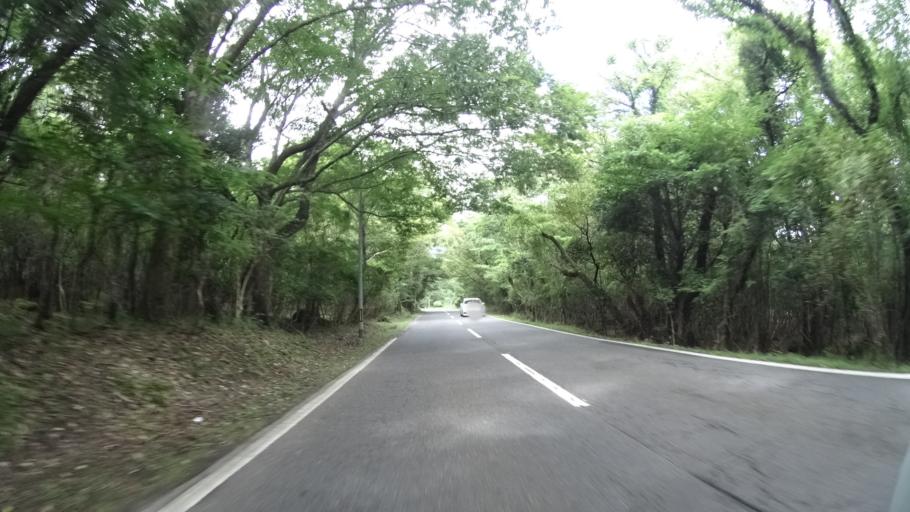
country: JP
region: Oita
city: Beppu
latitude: 33.3024
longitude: 131.3855
